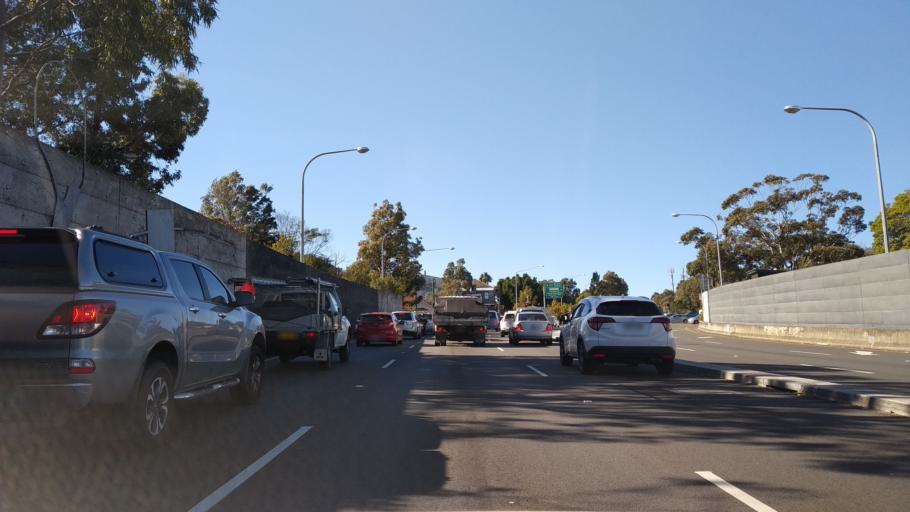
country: AU
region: New South Wales
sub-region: Leichhardt
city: Leichhardt
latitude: -33.8748
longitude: 151.1539
